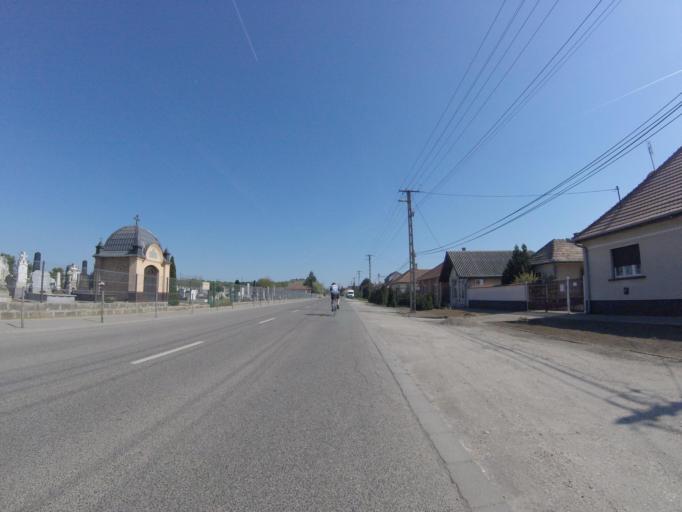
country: HU
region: Pest
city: Ujhartyan
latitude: 47.2163
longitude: 19.3894
